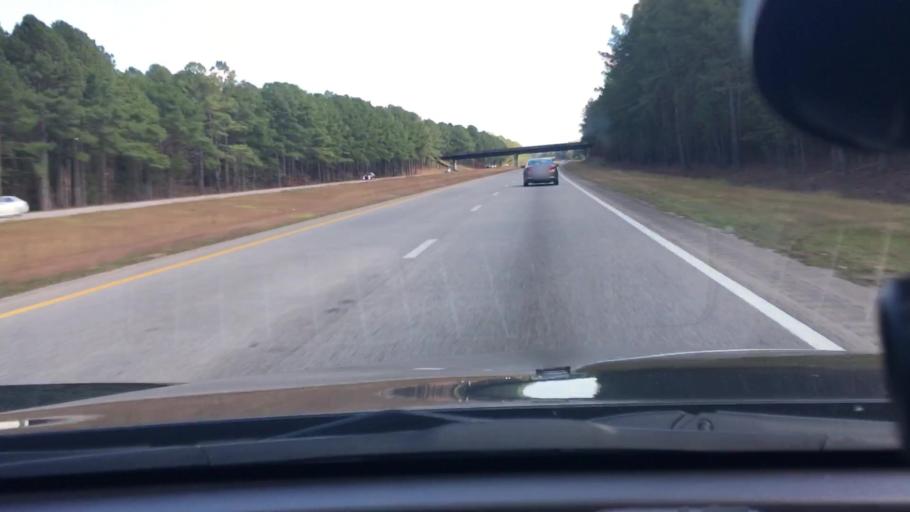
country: US
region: North Carolina
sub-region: Wilson County
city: Lucama
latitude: 35.7832
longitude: -78.0914
